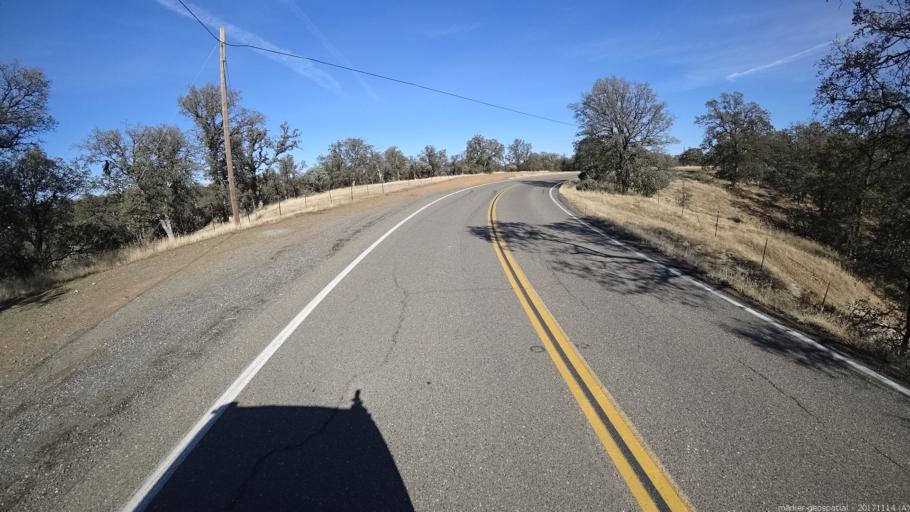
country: US
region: California
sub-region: Shasta County
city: Anderson
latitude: 40.4103
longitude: -122.3487
